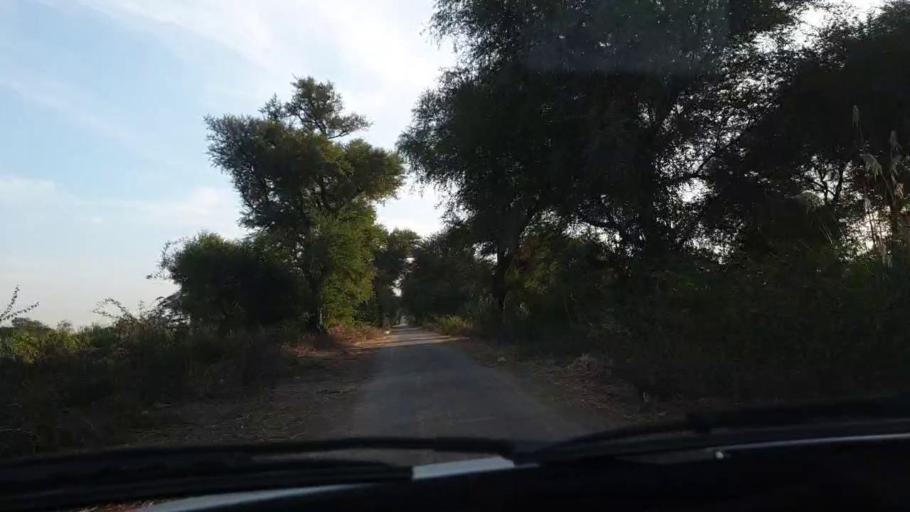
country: PK
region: Sindh
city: Bulri
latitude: 25.0221
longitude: 68.2887
